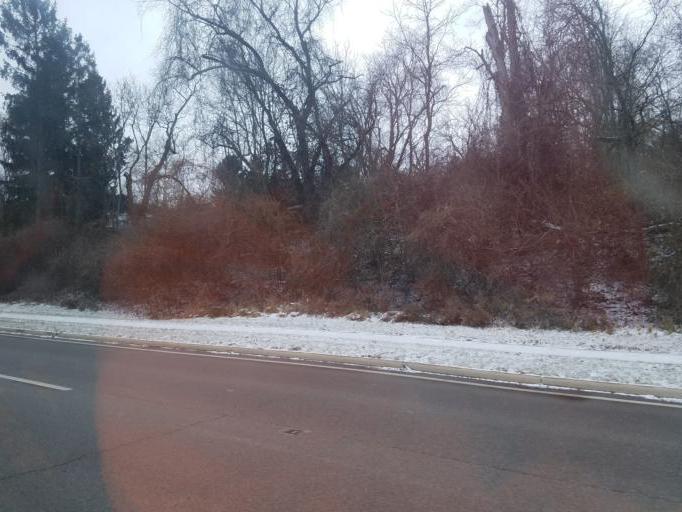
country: US
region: Ohio
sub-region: Franklin County
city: Worthington
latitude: 40.1192
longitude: -83.0351
